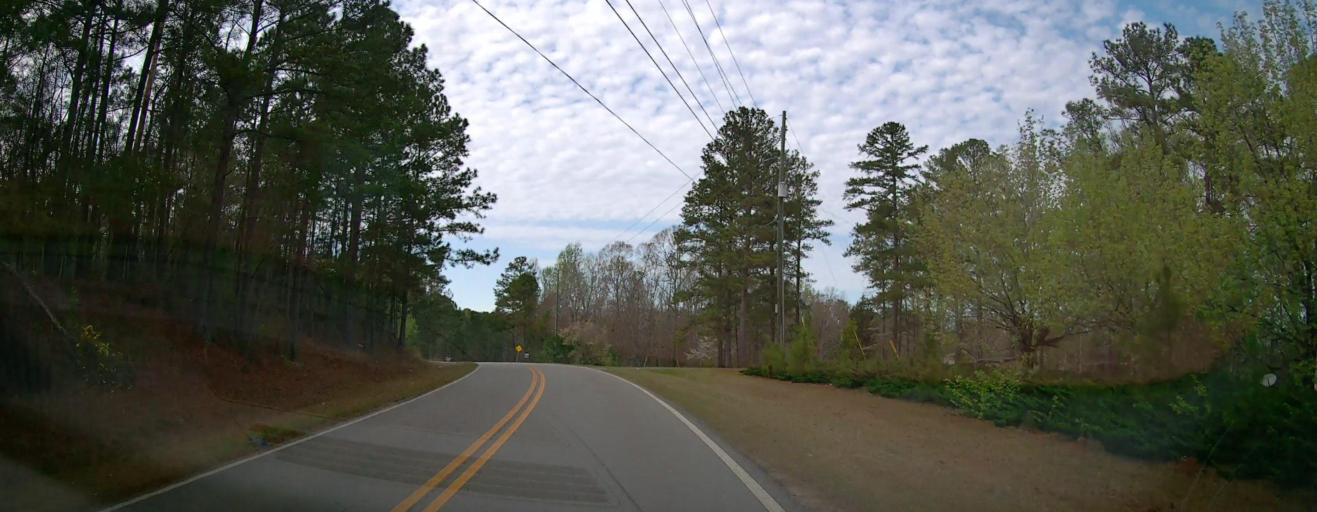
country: US
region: Georgia
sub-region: Bibb County
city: Macon
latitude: 32.9504
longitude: -83.6501
